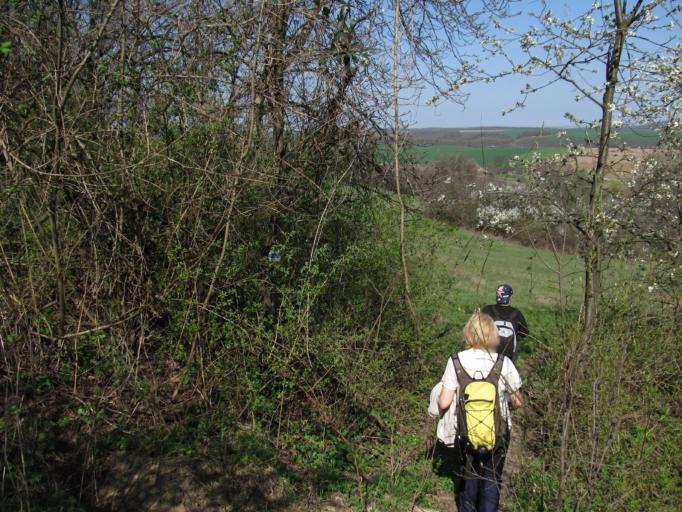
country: HU
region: Nograd
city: Retsag
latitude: 47.8805
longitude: 19.1869
